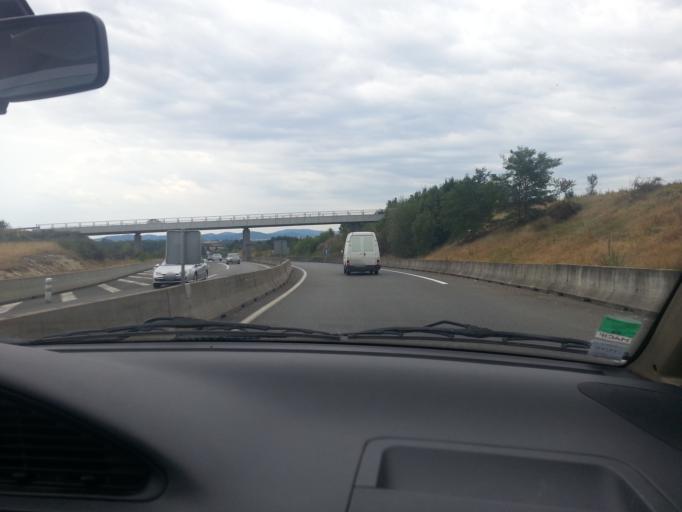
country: FR
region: Auvergne
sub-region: Departement de l'Allier
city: Lapalisse
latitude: 46.2422
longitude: 3.6177
